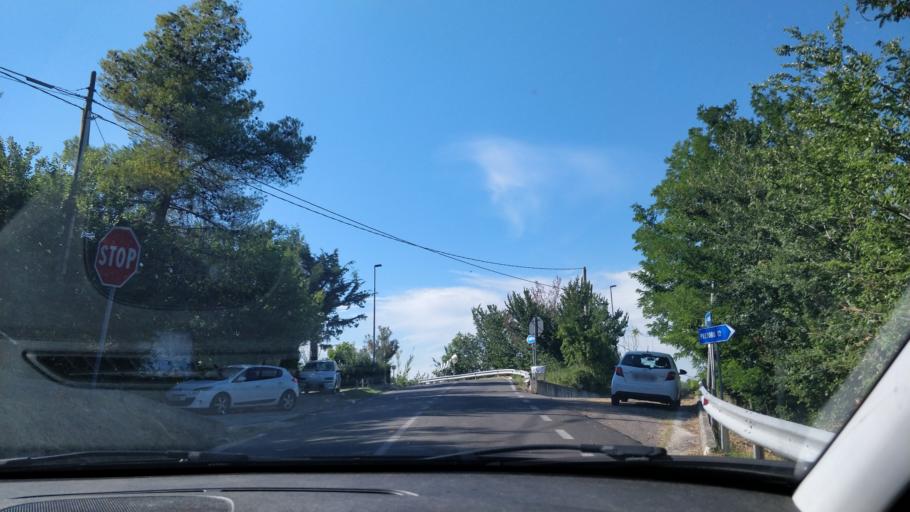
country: IT
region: Abruzzo
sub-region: Provincia di Pescara
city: Serramonacesca
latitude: 42.2555
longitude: 14.0904
